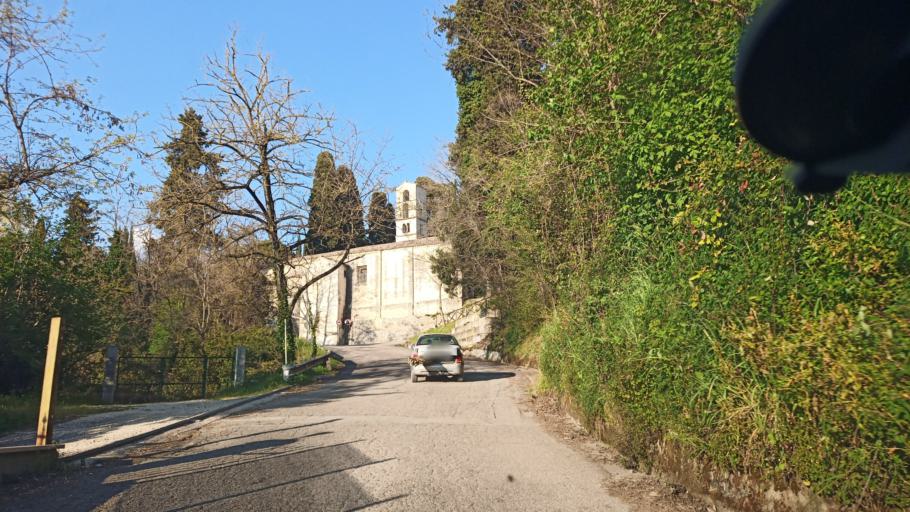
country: IT
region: Latium
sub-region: Provincia di Rieti
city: Poggio Mirteto
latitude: 42.2674
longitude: 12.6849
